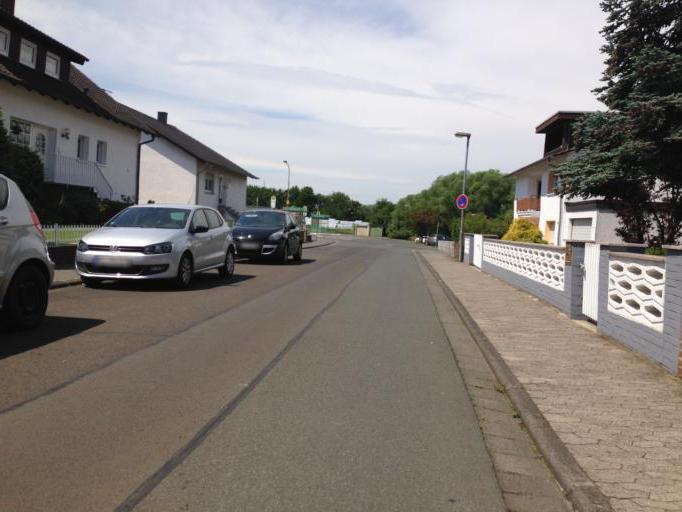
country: DE
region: Hesse
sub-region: Regierungsbezirk Giessen
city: Grossen Buseck
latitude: 50.6041
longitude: 8.7747
